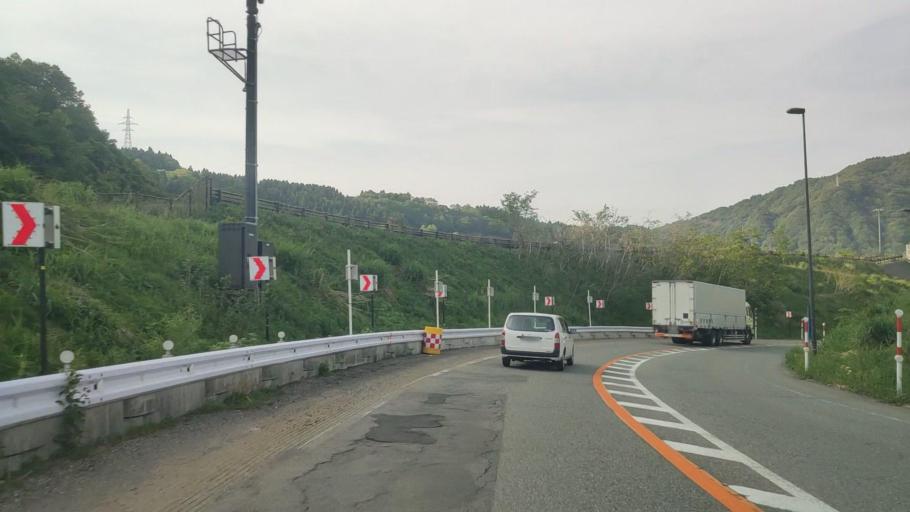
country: JP
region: Toyama
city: Yatsuomachi-higashikumisaka
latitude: 36.5345
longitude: 137.2258
